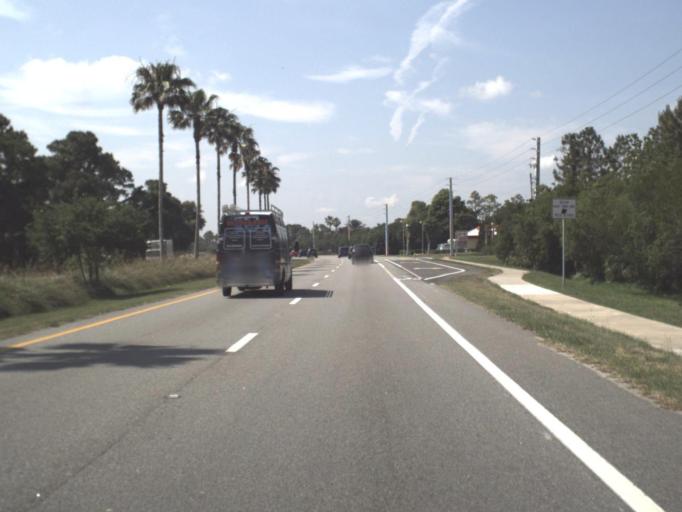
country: US
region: Florida
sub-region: Saint Johns County
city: Ponte Vedra Beach
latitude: 30.2435
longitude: -81.3877
